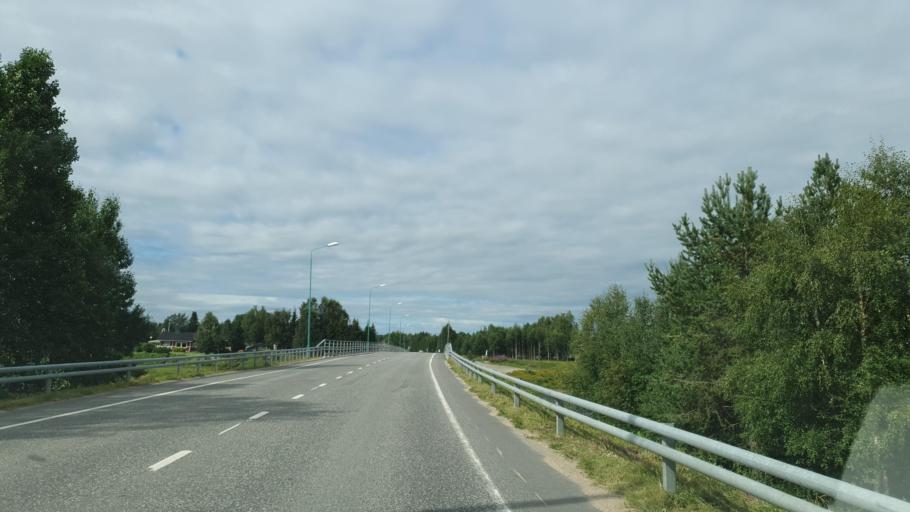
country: FI
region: Lapland
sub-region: Tunturi-Lappi
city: Kittilae
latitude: 67.6468
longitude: 24.9330
